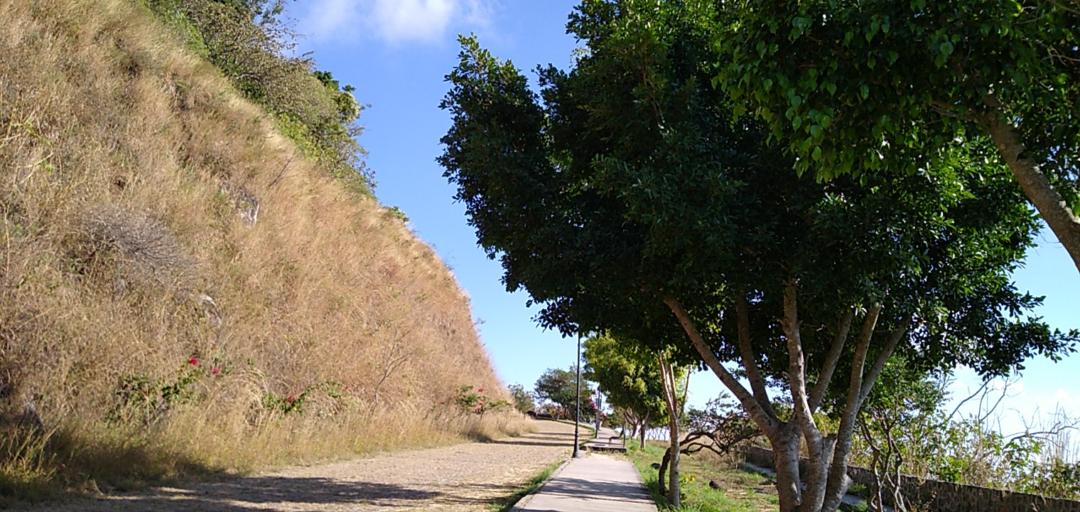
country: MX
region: Nayarit
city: Tepic
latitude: 21.5346
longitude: -104.8848
